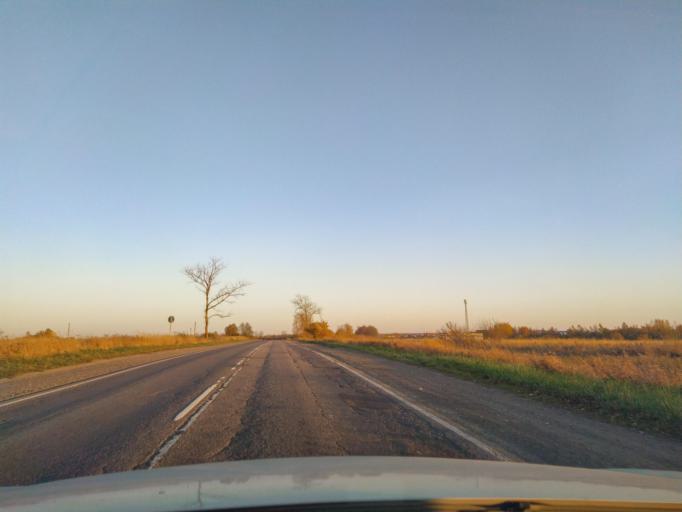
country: RU
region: Leningrad
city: Maloye Verevo
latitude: 59.6080
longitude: 30.2444
